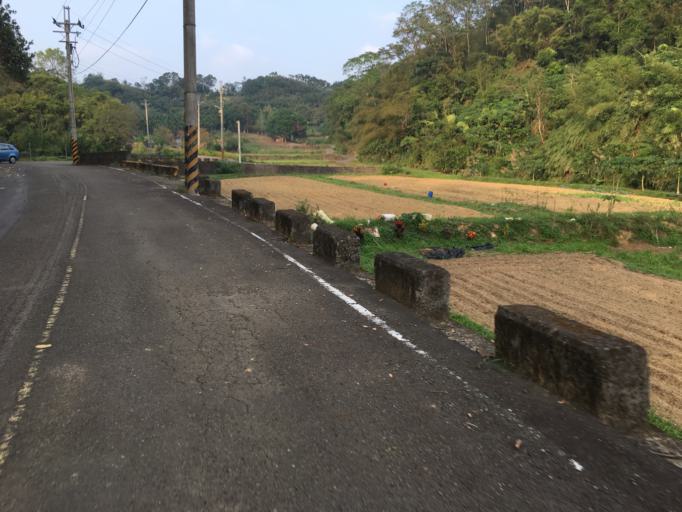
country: TW
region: Taiwan
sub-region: Hsinchu
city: Hsinchu
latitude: 24.7165
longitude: 121.0588
